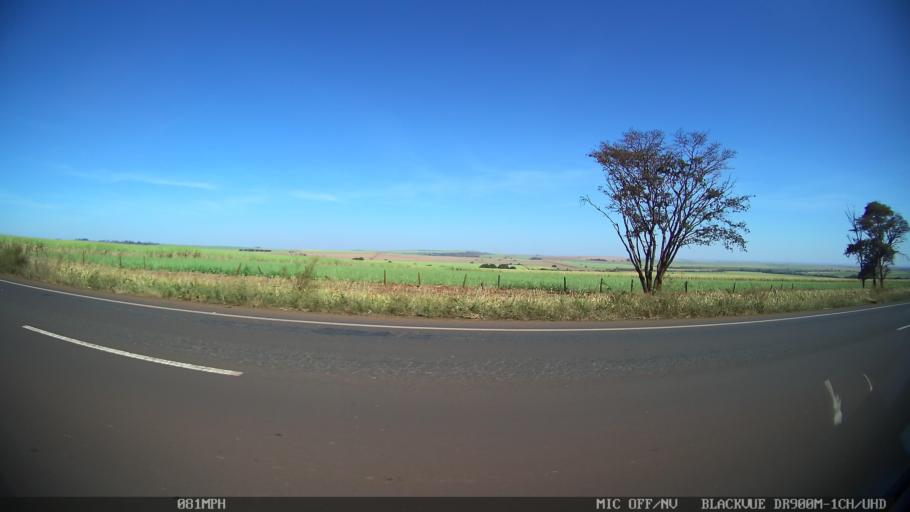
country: BR
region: Sao Paulo
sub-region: Ipua
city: Ipua
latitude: -20.4733
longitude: -48.1016
